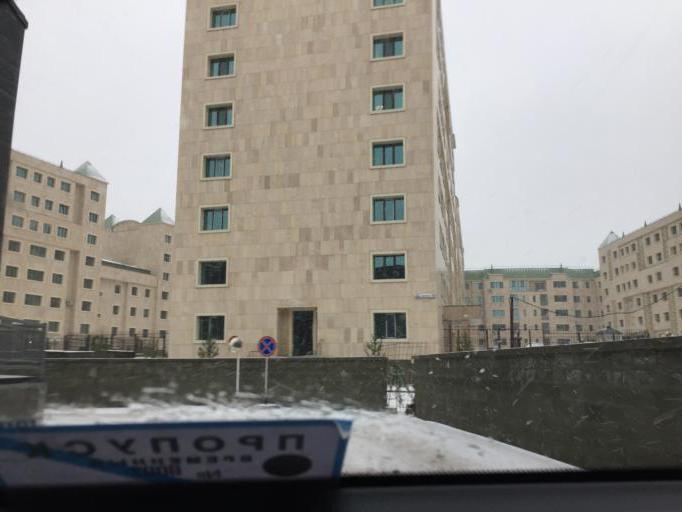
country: KZ
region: Astana Qalasy
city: Astana
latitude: 51.1384
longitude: 71.4117
